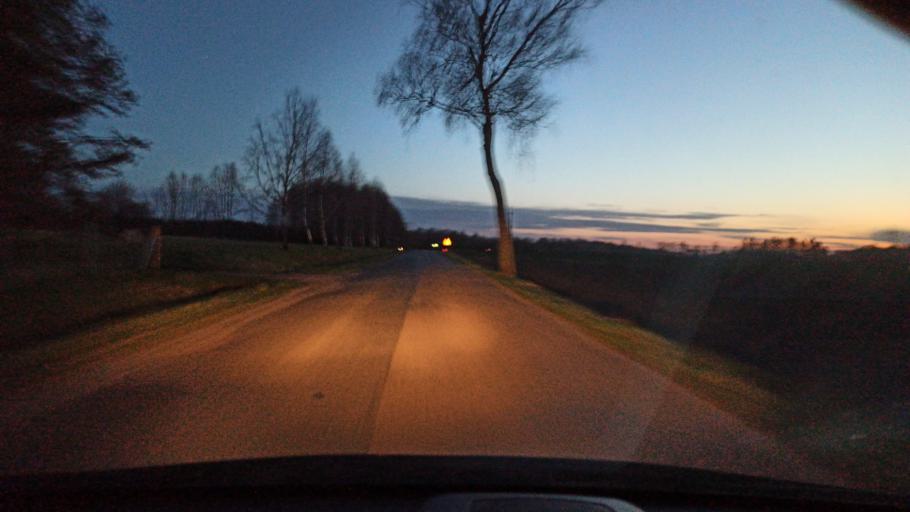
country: PL
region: Warmian-Masurian Voivodeship
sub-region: Powiat elblaski
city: Gronowo Gorne
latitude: 54.1734
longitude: 19.5096
